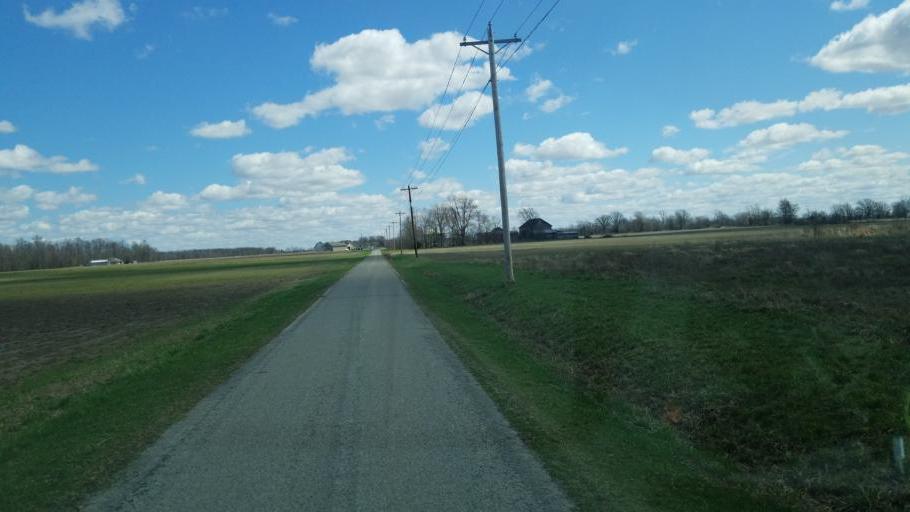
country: US
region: Ohio
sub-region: Hancock County
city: Arlington
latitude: 40.9537
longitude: -83.5302
